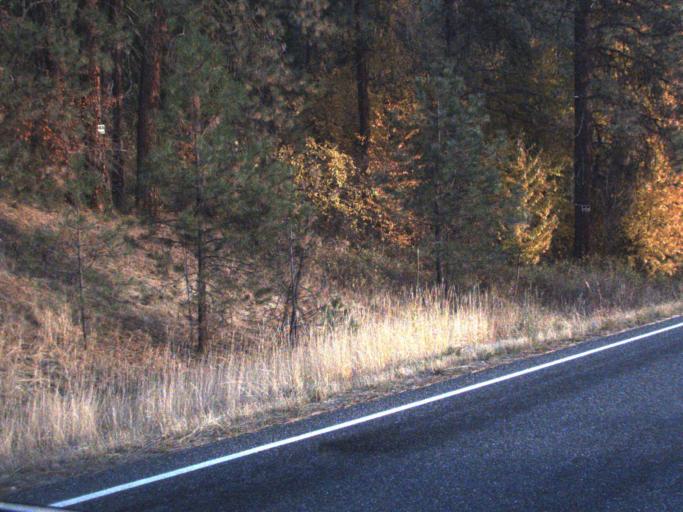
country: US
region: Washington
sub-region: Stevens County
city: Kettle Falls
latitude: 48.6949
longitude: -118.0130
